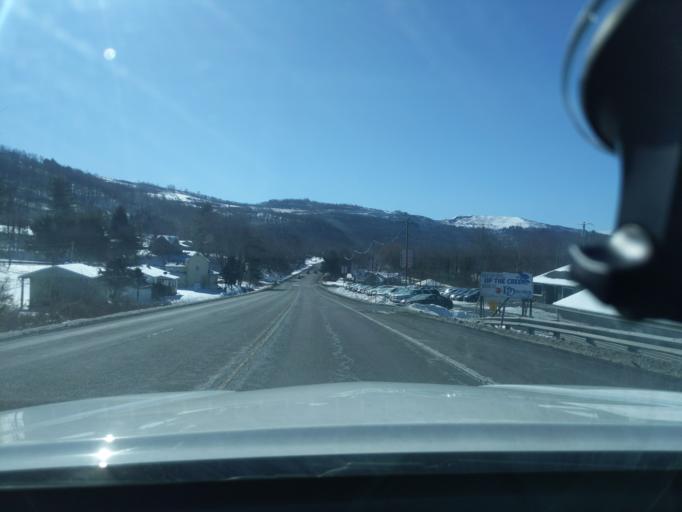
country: US
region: Maryland
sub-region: Allegany County
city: Westernport
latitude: 39.5248
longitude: -79.0175
